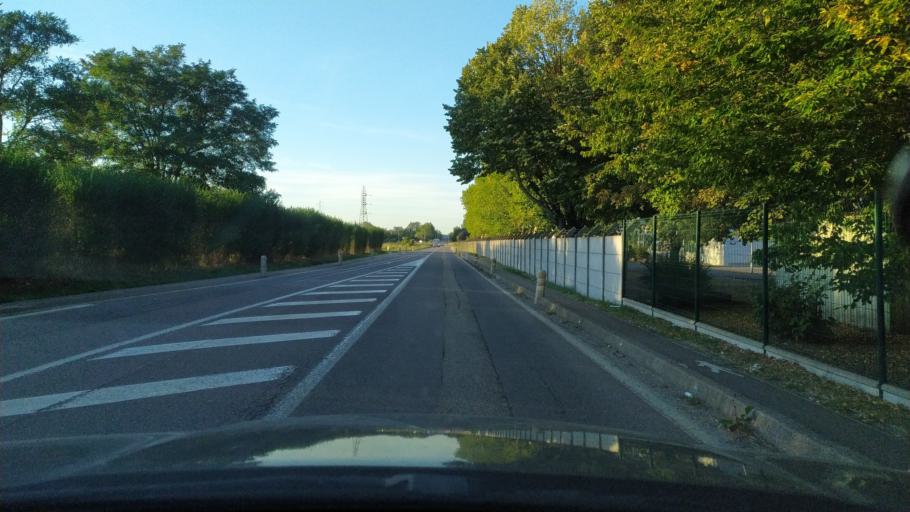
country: FR
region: Lorraine
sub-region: Departement de la Moselle
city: Maizieres-les-Metz
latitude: 49.1991
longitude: 6.1497
